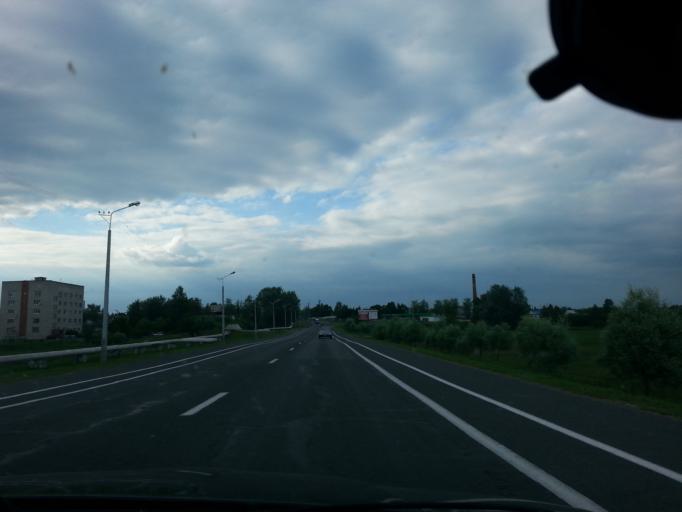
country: BY
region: Minsk
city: Myadzyel
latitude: 54.8796
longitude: 26.9400
